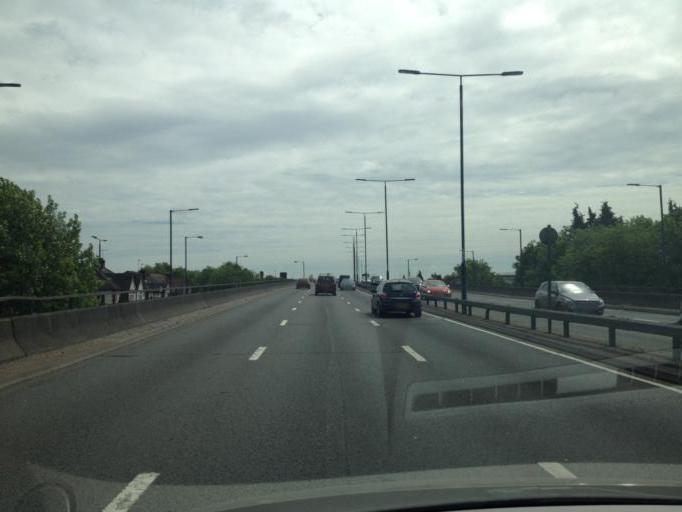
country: GB
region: England
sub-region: Greater London
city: Greenford
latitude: 51.5367
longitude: -0.3495
